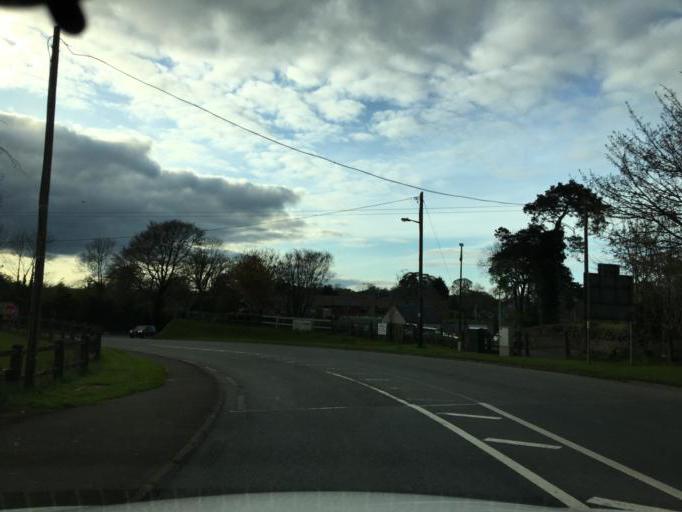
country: IE
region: Leinster
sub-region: Loch Garman
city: New Ross
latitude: 52.4136
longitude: -6.9360
